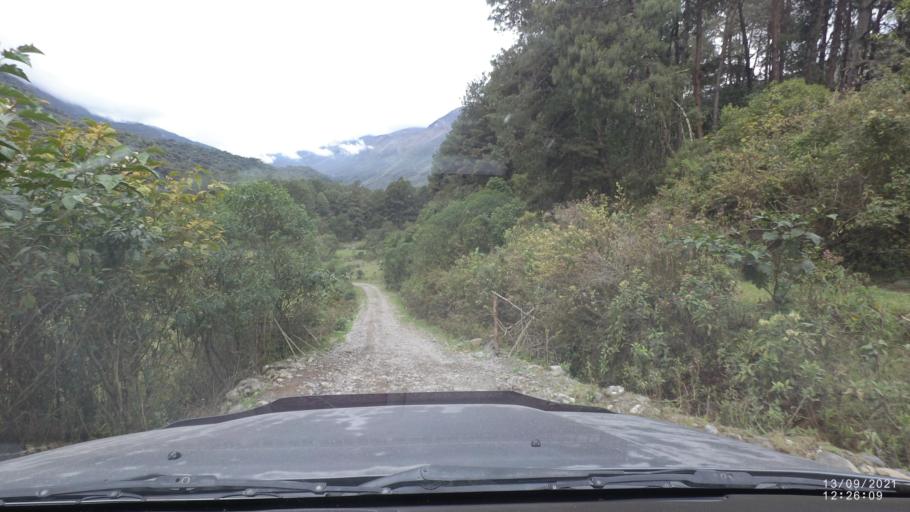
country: BO
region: Cochabamba
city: Colomi
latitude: -17.2528
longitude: -65.8167
